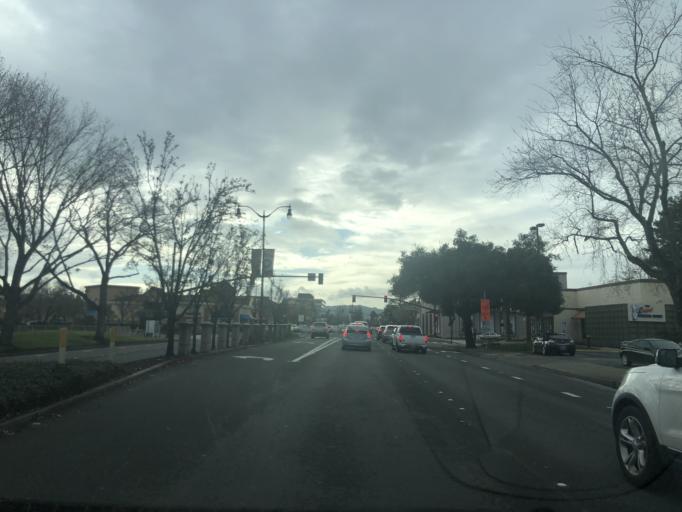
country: US
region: California
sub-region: Contra Costa County
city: Pleasant Hill
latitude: 37.9488
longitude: -122.0602
